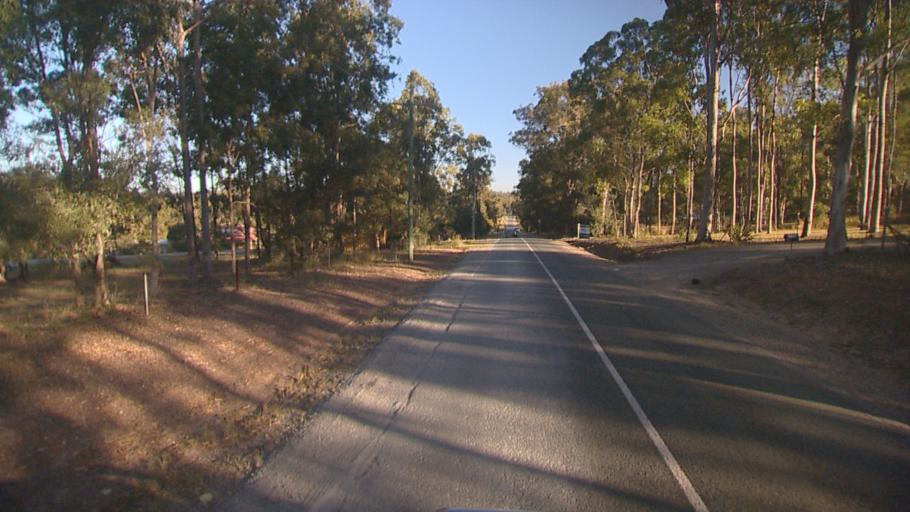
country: AU
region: Queensland
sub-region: Logan
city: Chambers Flat
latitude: -27.7779
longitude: 153.1361
